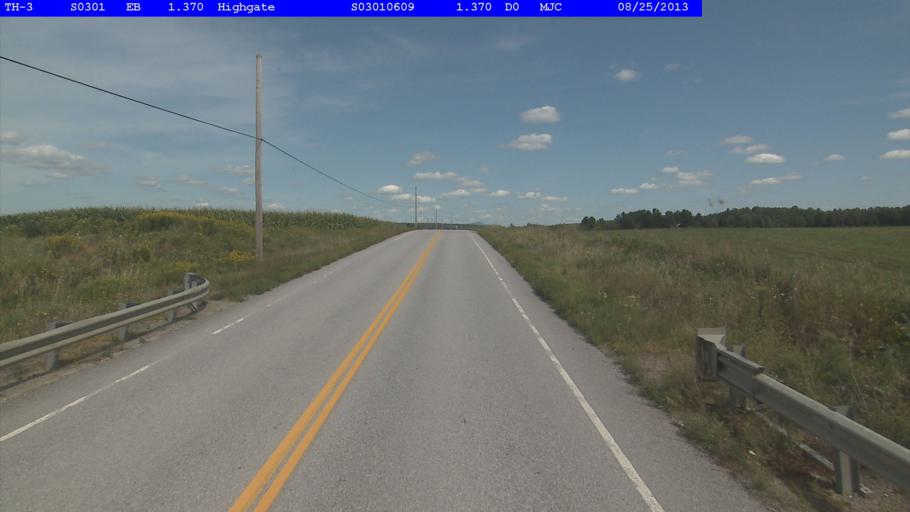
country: US
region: Vermont
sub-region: Franklin County
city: Swanton
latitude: 44.9581
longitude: -72.9931
